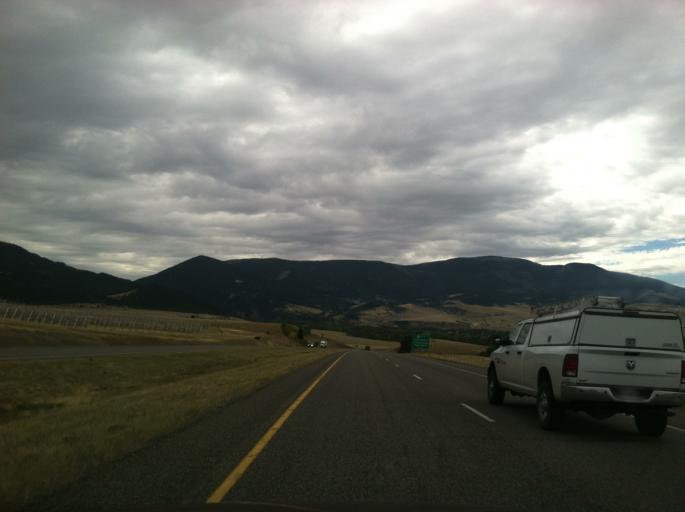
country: US
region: Montana
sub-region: Park County
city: Livingston
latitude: 45.6485
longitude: -110.5475
